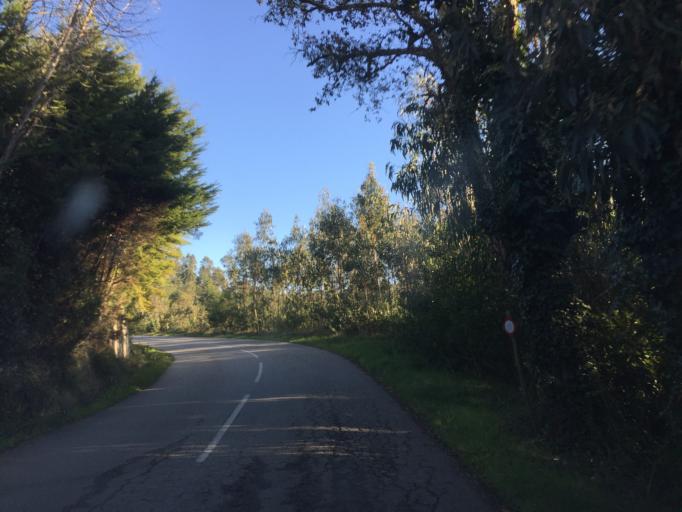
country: PT
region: Coimbra
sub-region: Figueira da Foz
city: Alhadas
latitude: 40.1618
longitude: -8.8046
